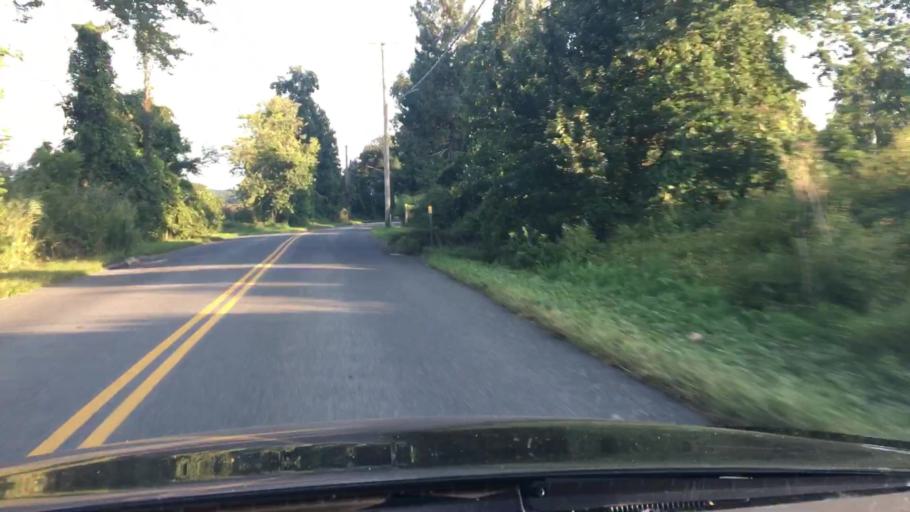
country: US
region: Connecticut
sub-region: Litchfield County
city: New Milford
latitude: 41.5962
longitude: -73.3719
